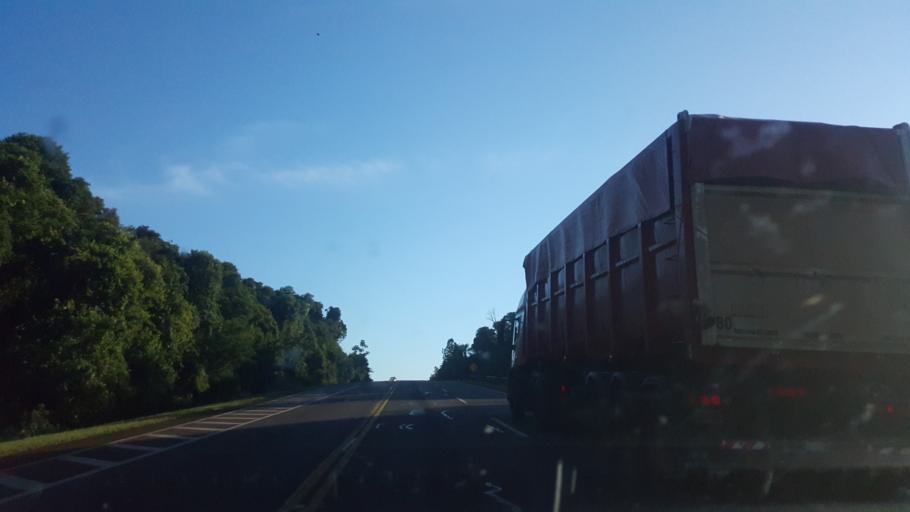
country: AR
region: Misiones
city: El Alcazar
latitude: -26.6963
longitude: -54.8344
